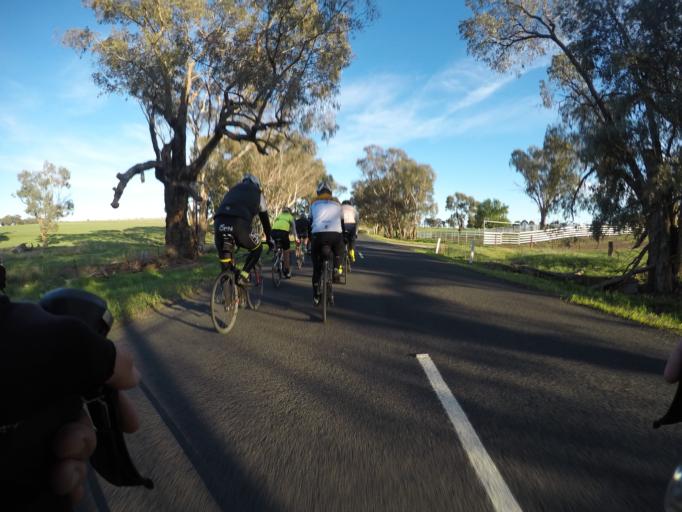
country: AU
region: New South Wales
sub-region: Cabonne
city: Molong
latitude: -33.0390
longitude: 148.8117
